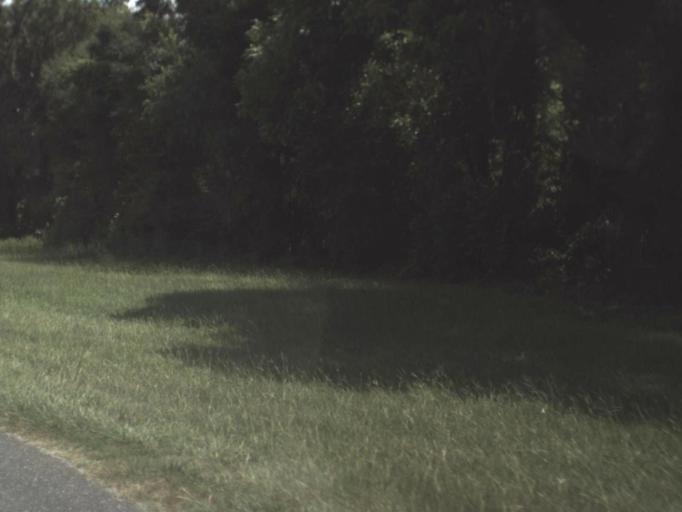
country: US
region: Florida
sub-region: Columbia County
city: Lake City
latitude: 30.1222
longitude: -82.6199
